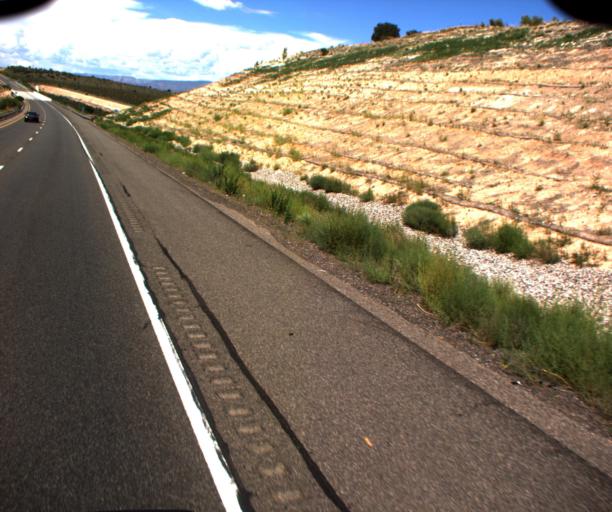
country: US
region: Arizona
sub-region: Yavapai County
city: Verde Village
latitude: 34.6757
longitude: -111.9706
